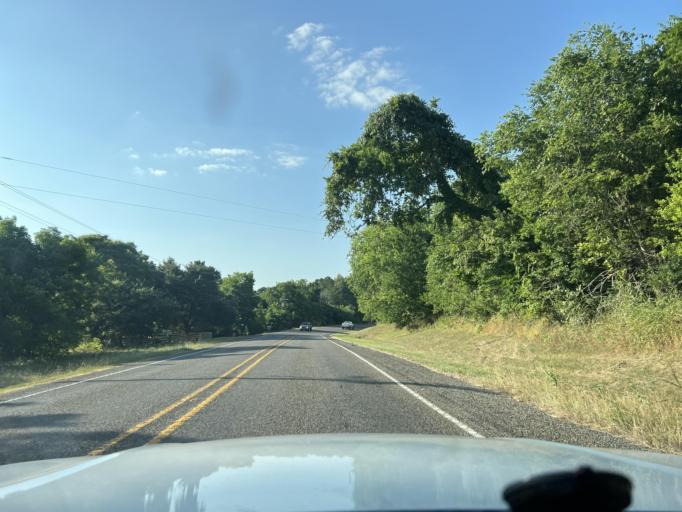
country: US
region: Texas
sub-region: Washington County
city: Brenham
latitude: 30.1490
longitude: -96.2574
